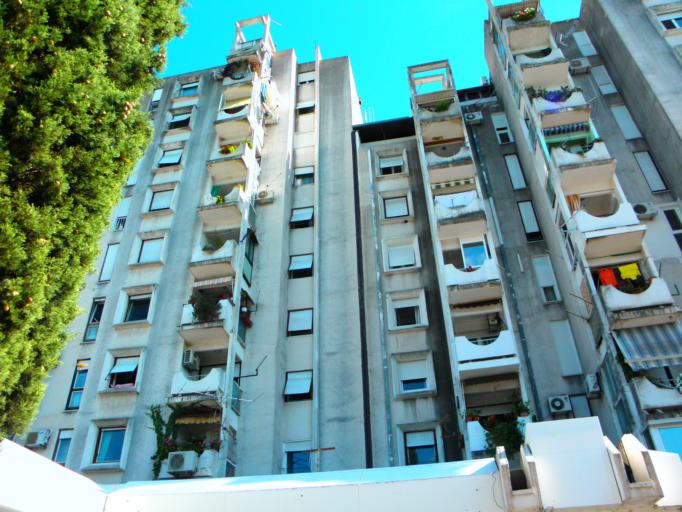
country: HR
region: Dubrovacko-Neretvanska
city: Komin
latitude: 43.0522
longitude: 17.4358
